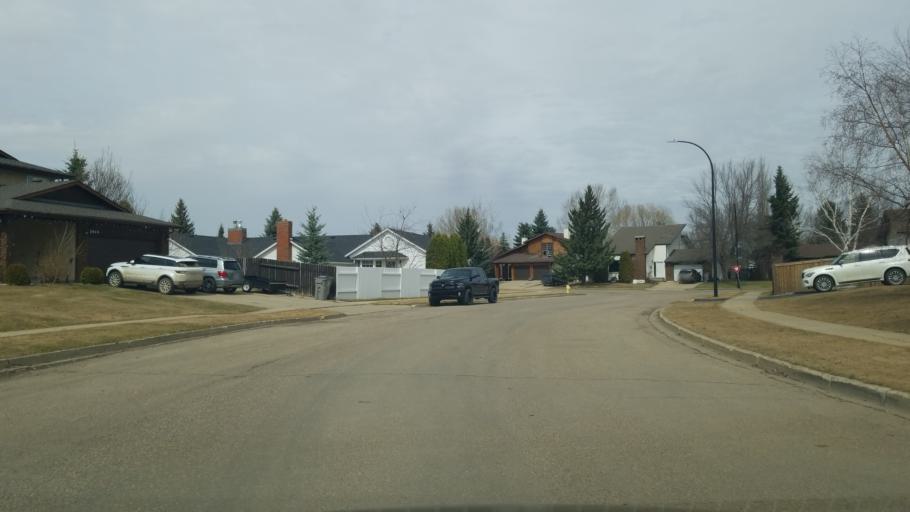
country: CA
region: Saskatchewan
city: Lloydminster
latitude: 53.2659
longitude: -110.0285
